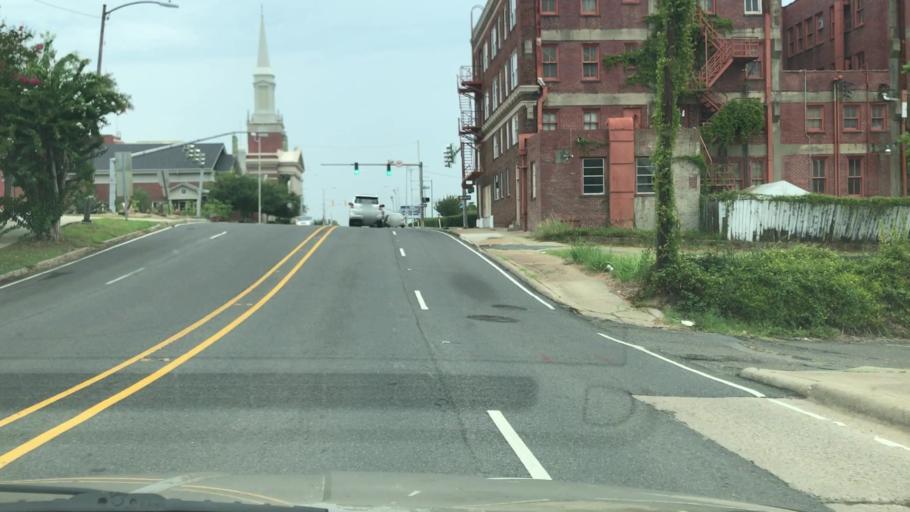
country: US
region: Louisiana
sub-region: Caddo Parish
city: Shreveport
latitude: 32.5095
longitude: -93.7512
